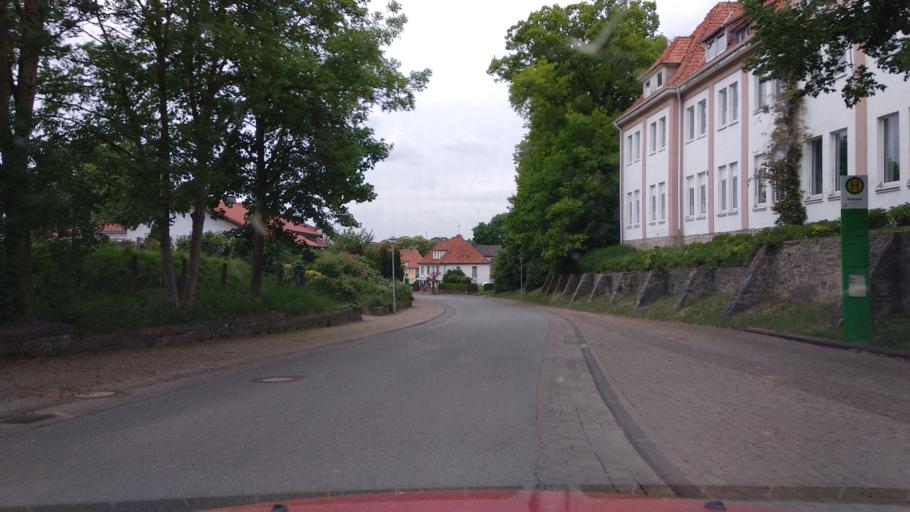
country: DE
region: North Rhine-Westphalia
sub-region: Regierungsbezirk Detmold
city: Willebadessen
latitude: 51.5947
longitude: 9.1319
